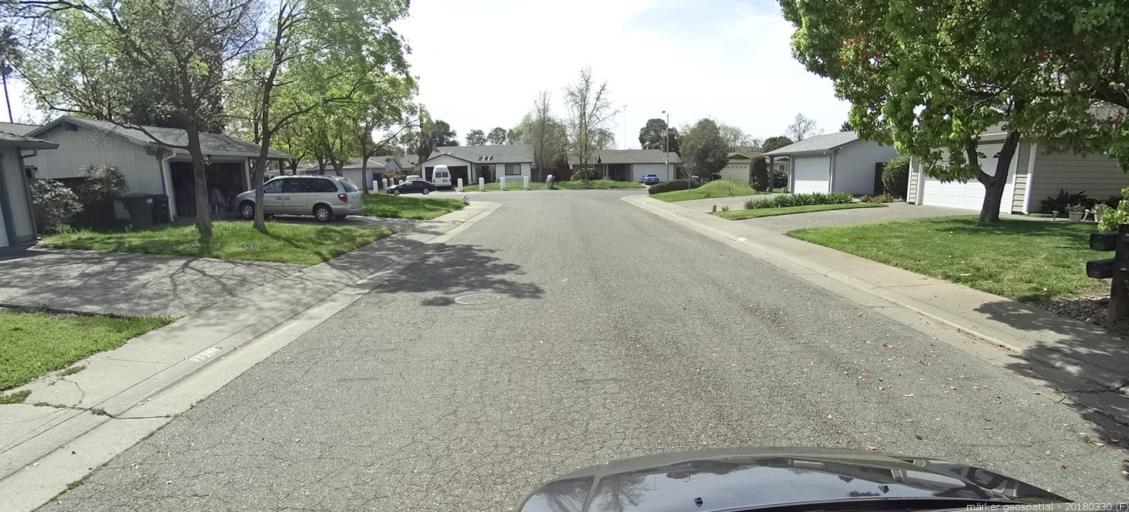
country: US
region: California
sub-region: Sacramento County
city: Rosemont
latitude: 38.5456
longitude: -121.3672
